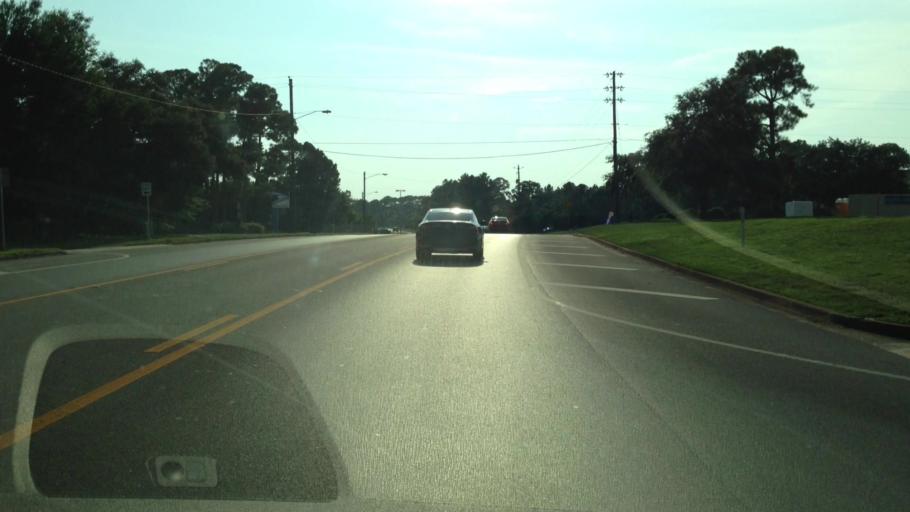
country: US
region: Florida
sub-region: Okaloosa County
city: Mary Esther
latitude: 30.4138
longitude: -86.6656
